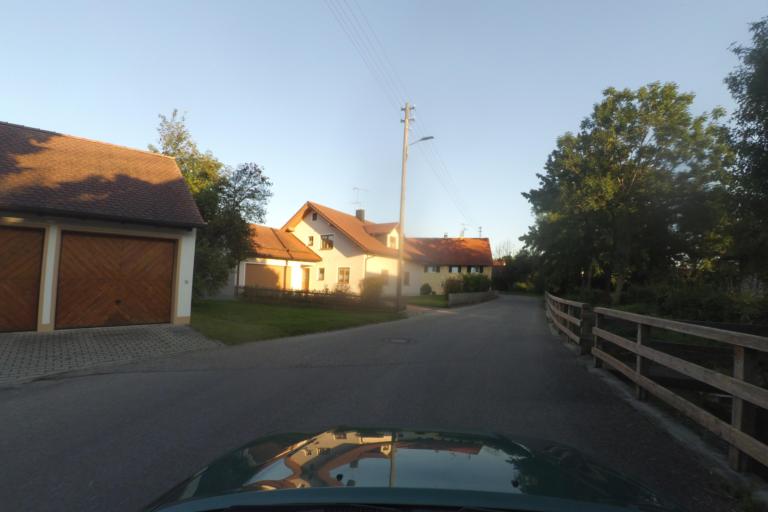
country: DE
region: Bavaria
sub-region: Upper Bavaria
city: Weil
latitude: 48.0991
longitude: 10.9073
